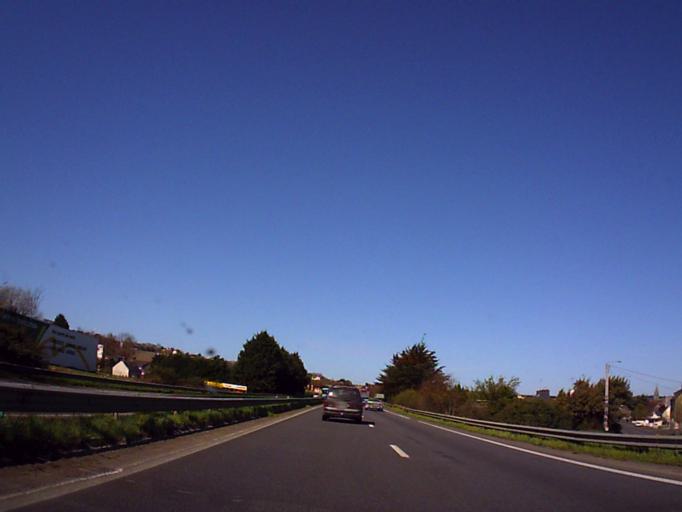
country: FR
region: Brittany
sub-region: Departement des Cotes-d'Armor
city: Yffiniac
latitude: 48.4794
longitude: -2.6691
